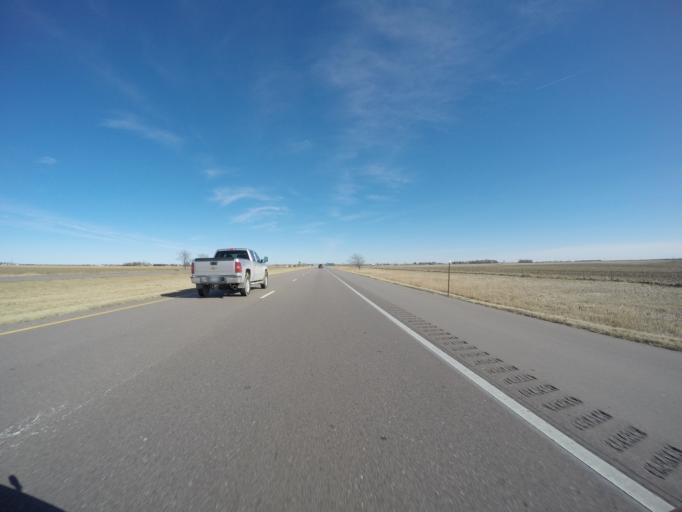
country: US
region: Nebraska
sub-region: York County
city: York
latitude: 40.8211
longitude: -97.6289
